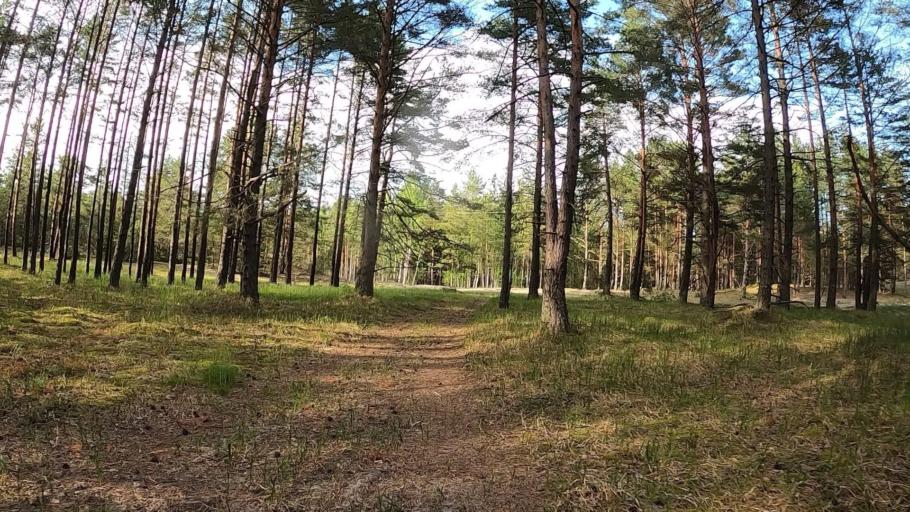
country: LV
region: Riga
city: Jaunciems
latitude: 57.0611
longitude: 24.1286
